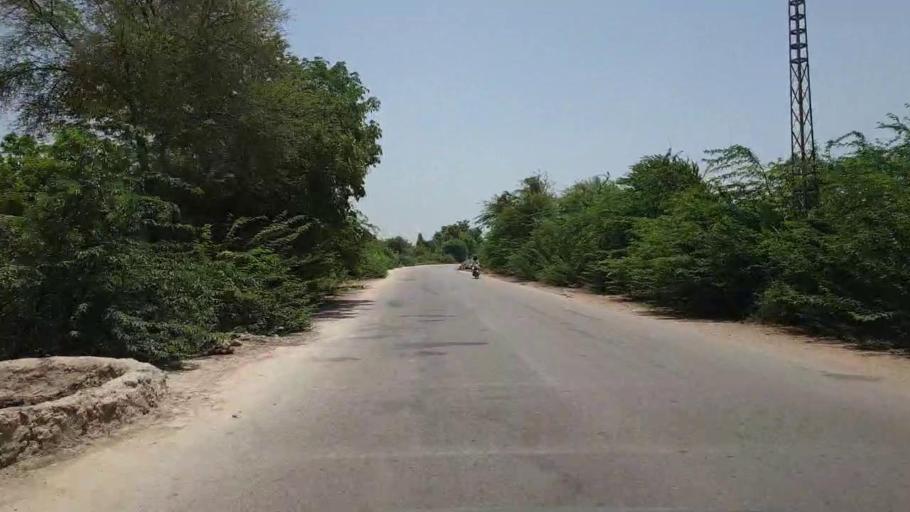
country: PK
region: Sindh
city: Sakrand
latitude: 26.1415
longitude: 68.3680
